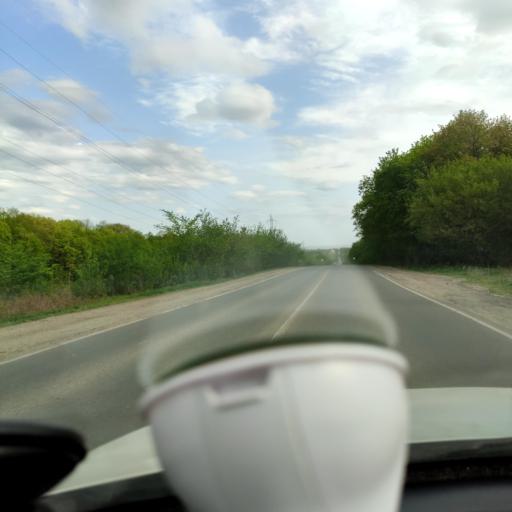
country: RU
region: Samara
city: Novosemeykino
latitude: 53.3306
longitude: 50.2572
